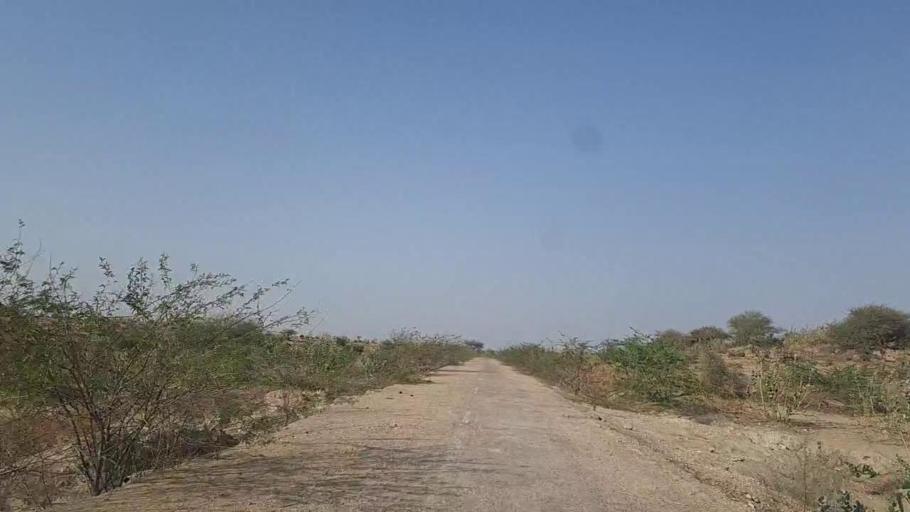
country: PK
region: Sindh
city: Naukot
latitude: 24.6180
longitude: 69.3477
